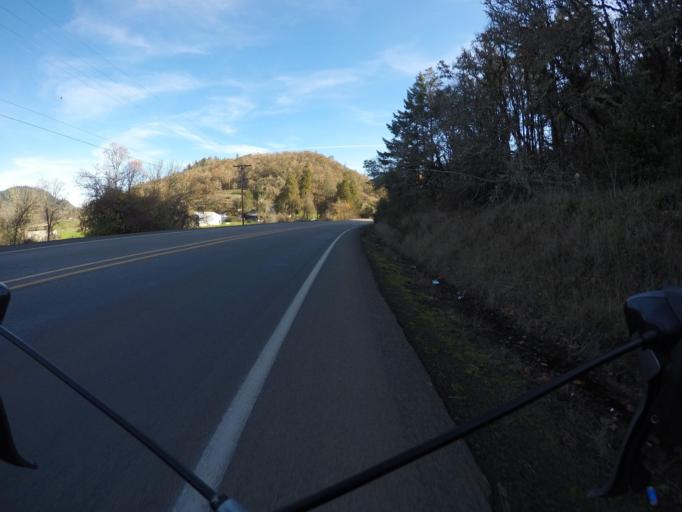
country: US
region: Oregon
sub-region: Douglas County
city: Winston
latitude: 43.1876
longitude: -123.4558
